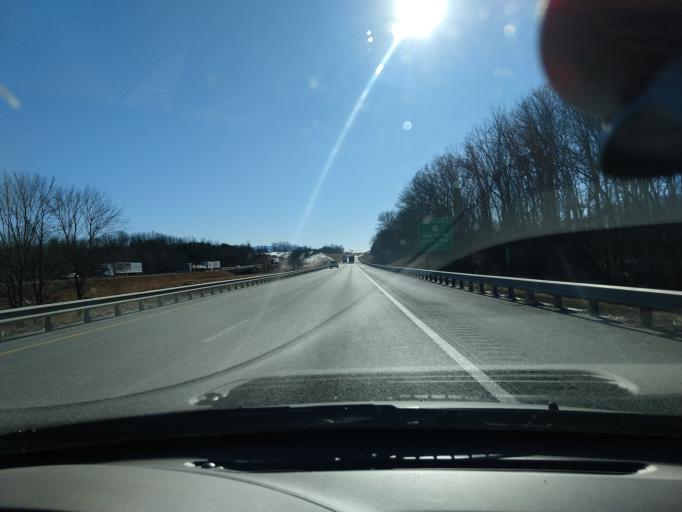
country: US
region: Virginia
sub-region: Augusta County
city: Jolivue
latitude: 38.0915
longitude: -79.0765
